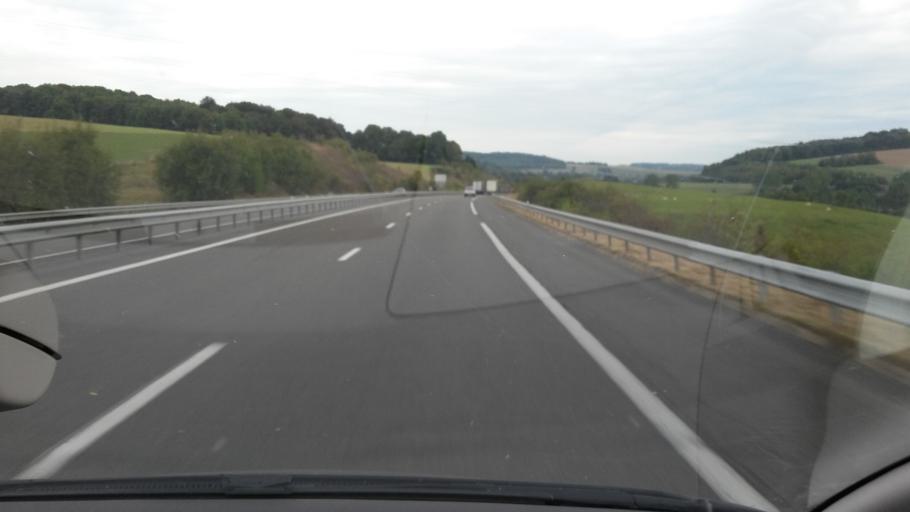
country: FR
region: Champagne-Ardenne
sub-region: Departement des Ardennes
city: La Francheville
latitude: 49.6575
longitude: 4.6351
